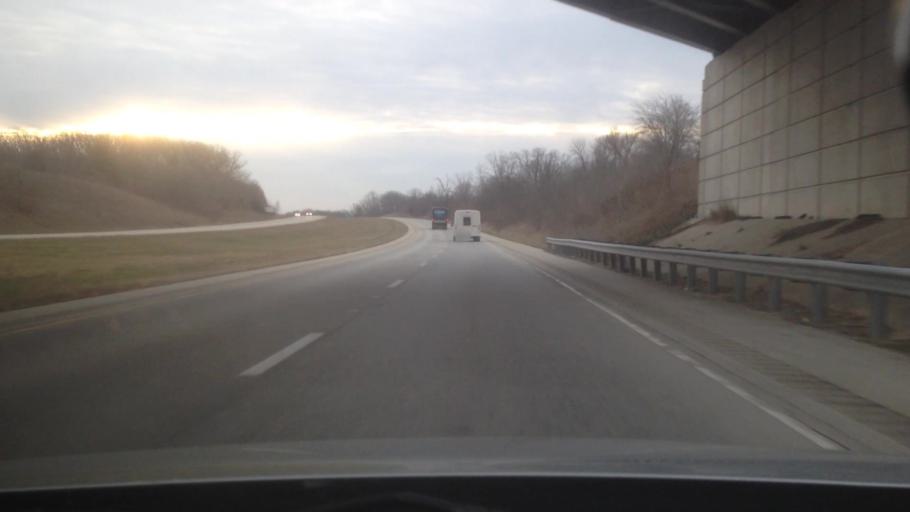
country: US
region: Illinois
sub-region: Macon County
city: Harristown
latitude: 39.8141
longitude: -89.0289
